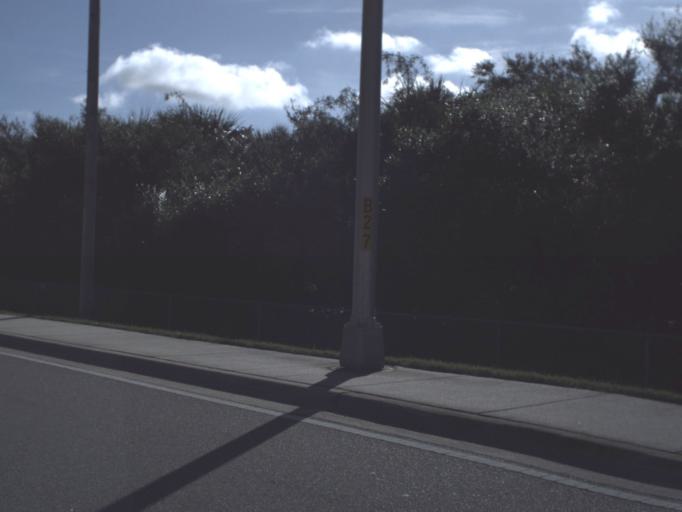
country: US
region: Florida
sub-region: Pinellas County
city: South Pasadena
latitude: 27.7514
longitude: -82.7394
